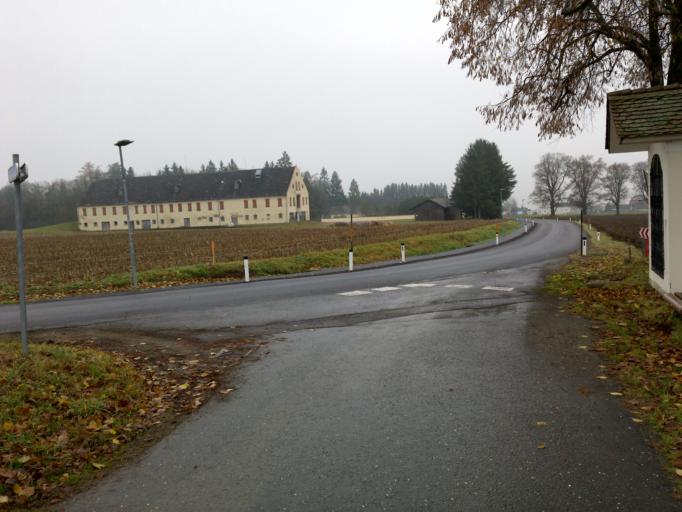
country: AT
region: Styria
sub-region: Politischer Bezirk Murtal
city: Sankt Marein bei Knittelfeld
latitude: 47.2825
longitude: 14.8599
